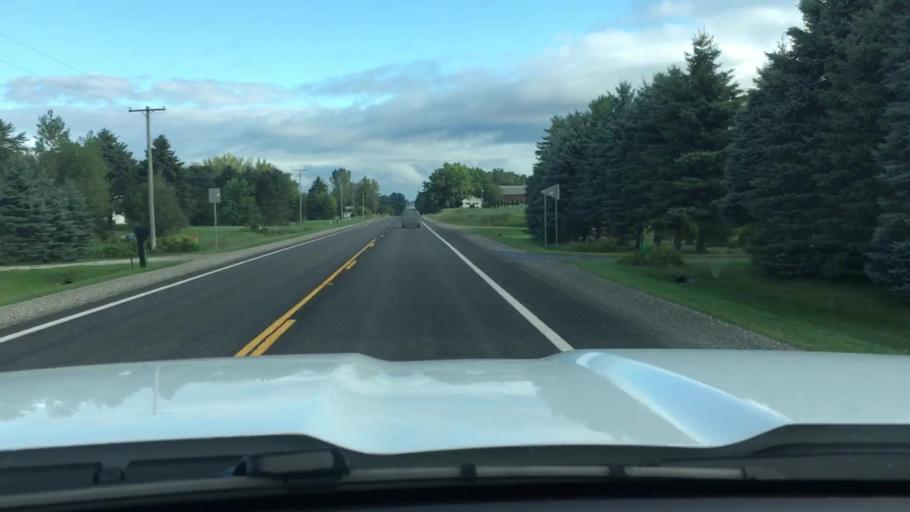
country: US
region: Michigan
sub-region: Tuscola County
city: Caro
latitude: 43.3515
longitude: -83.3827
